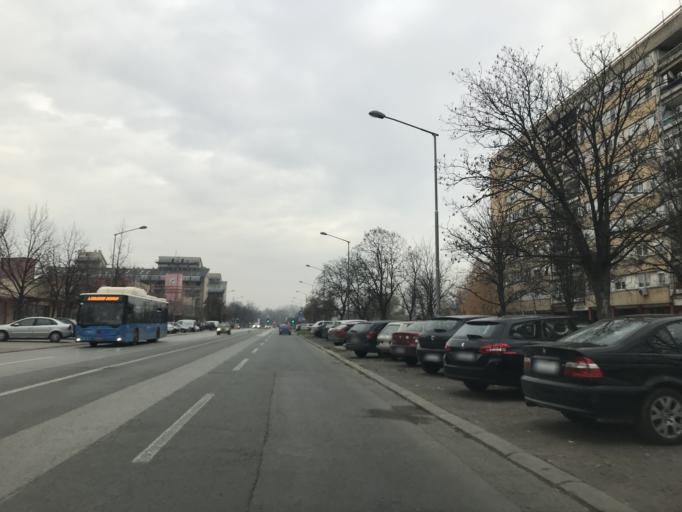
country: RS
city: Veternik
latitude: 45.2522
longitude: 19.7966
